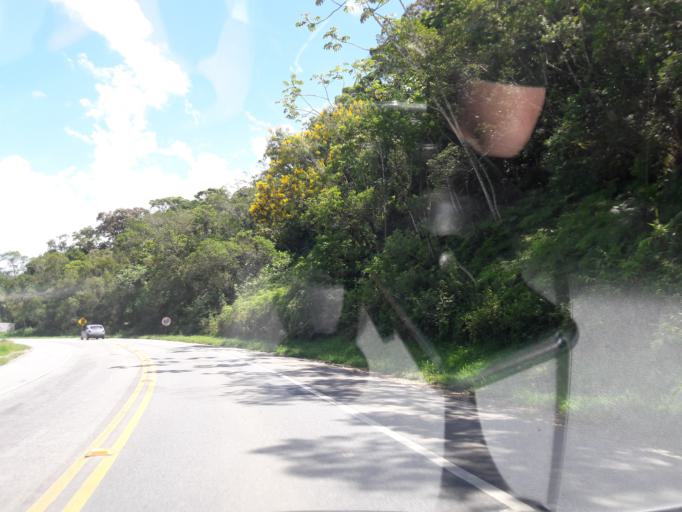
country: BR
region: Parana
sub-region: Antonina
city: Antonina
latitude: -25.4589
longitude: -48.8175
